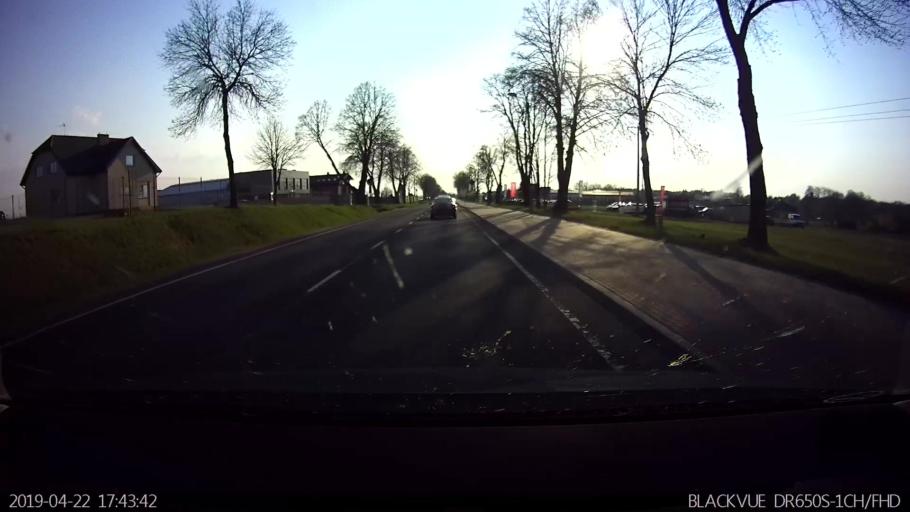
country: PL
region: Masovian Voivodeship
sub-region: Powiat wegrowski
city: Wegrow
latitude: 52.4042
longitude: 22.0583
